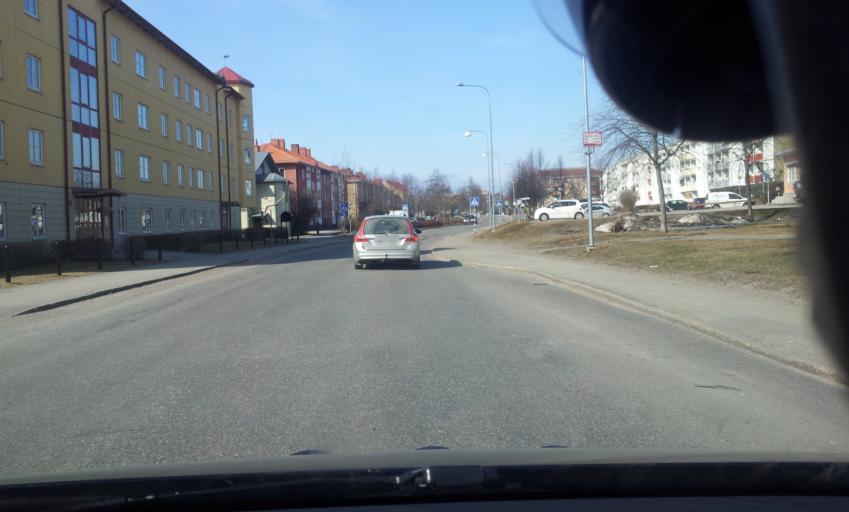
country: SE
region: Gaevleborg
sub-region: Ljusdals Kommun
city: Ljusdal
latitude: 61.8276
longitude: 16.1014
